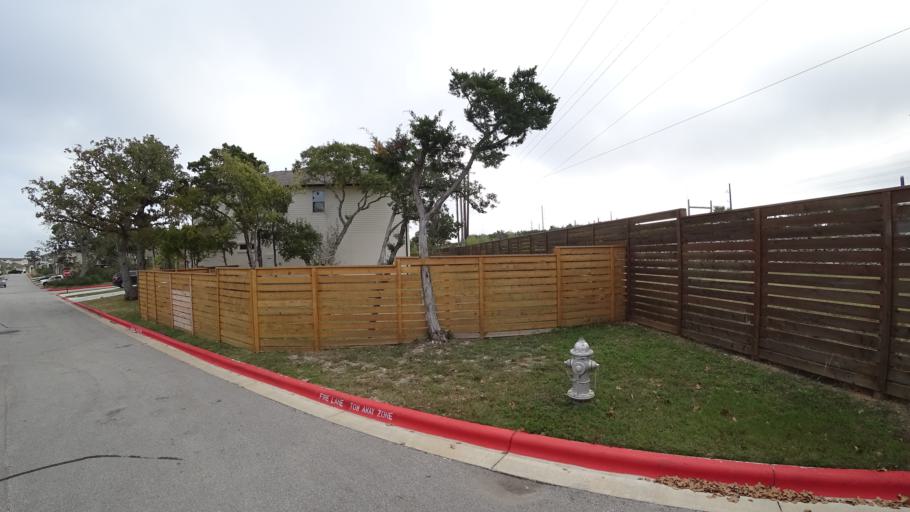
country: US
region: Texas
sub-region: Williamson County
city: Anderson Mill
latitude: 30.3994
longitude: -97.8440
